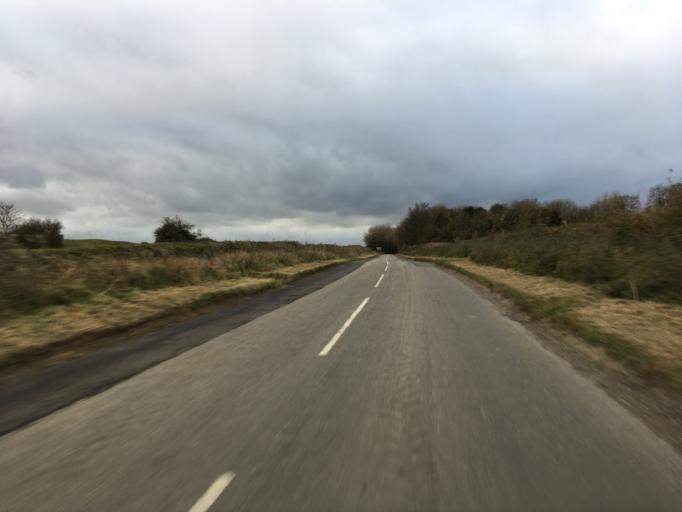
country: GB
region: England
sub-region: South Gloucestershire
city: Hinton
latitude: 51.4900
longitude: -2.3710
